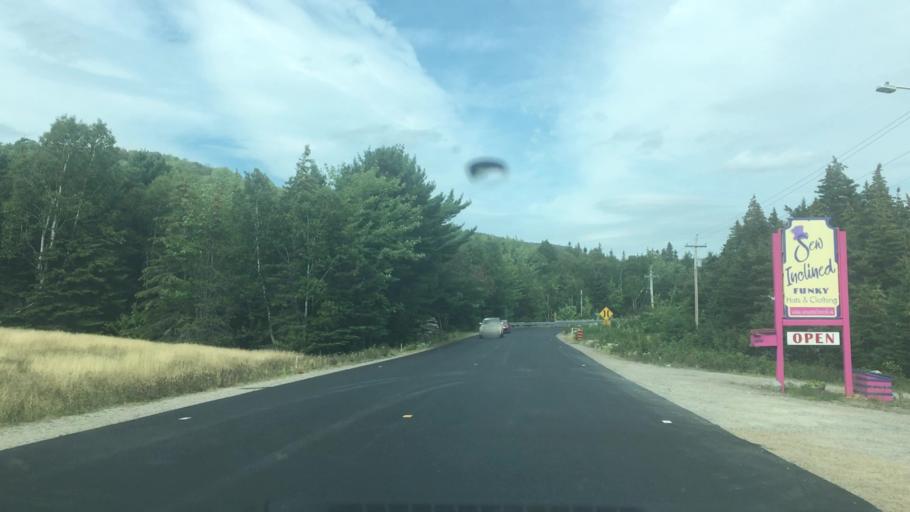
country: CA
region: Nova Scotia
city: Sydney Mines
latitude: 46.5453
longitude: -60.4155
